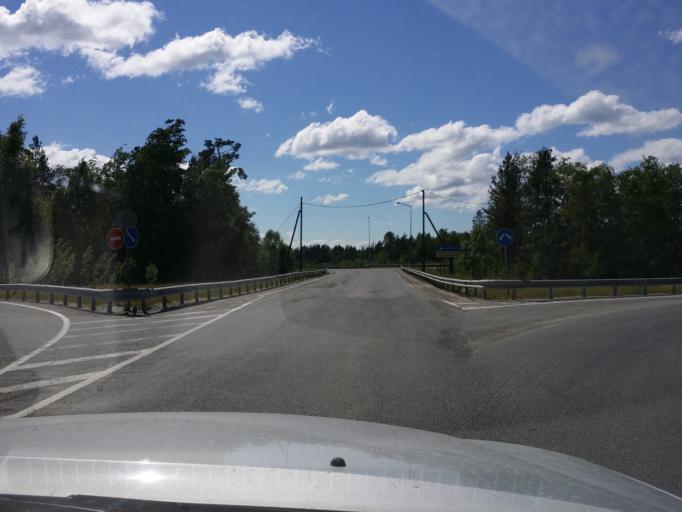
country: RU
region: Khanty-Mansiyskiy Avtonomnyy Okrug
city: Nizhnevartovsk
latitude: 61.0085
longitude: 76.4087
